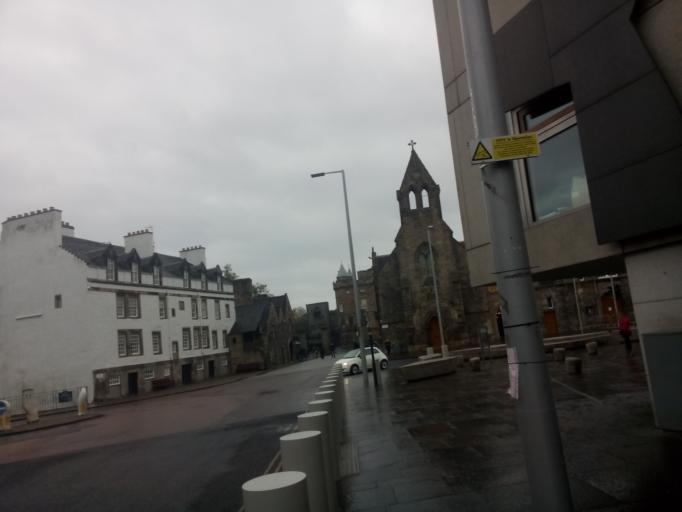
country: GB
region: Scotland
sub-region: Edinburgh
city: Edinburgh
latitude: 55.9527
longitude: -3.1747
